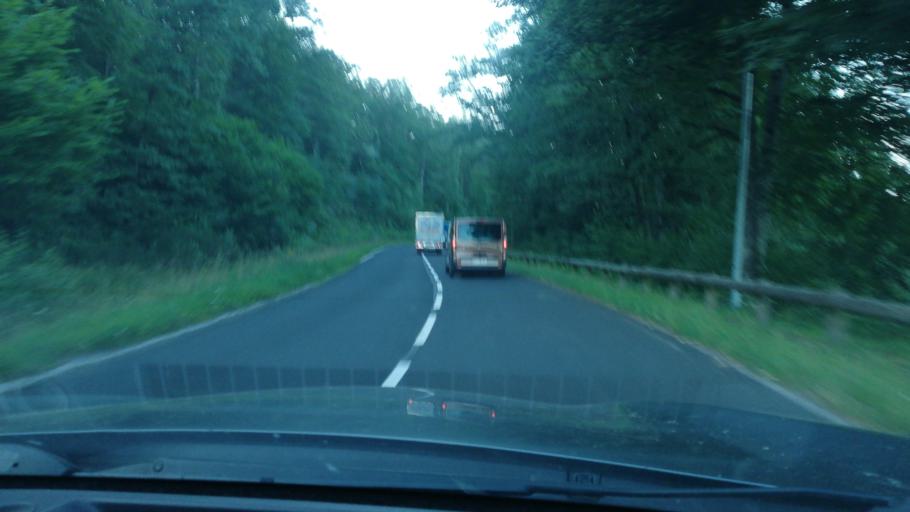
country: FR
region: Auvergne
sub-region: Departement du Cantal
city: Laroquebrou
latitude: 44.9282
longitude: 2.0765
